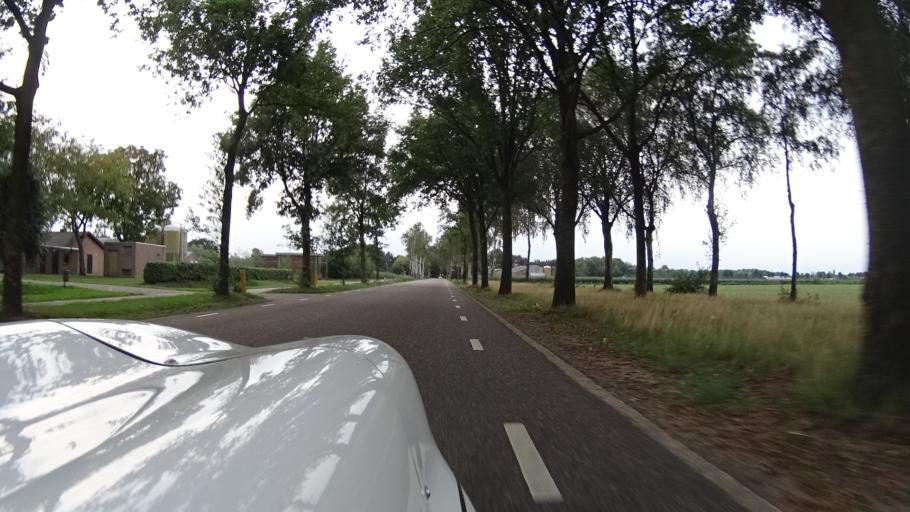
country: NL
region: North Brabant
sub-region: Gemeente Veghel
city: Mariaheide
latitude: 51.6294
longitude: 5.6081
